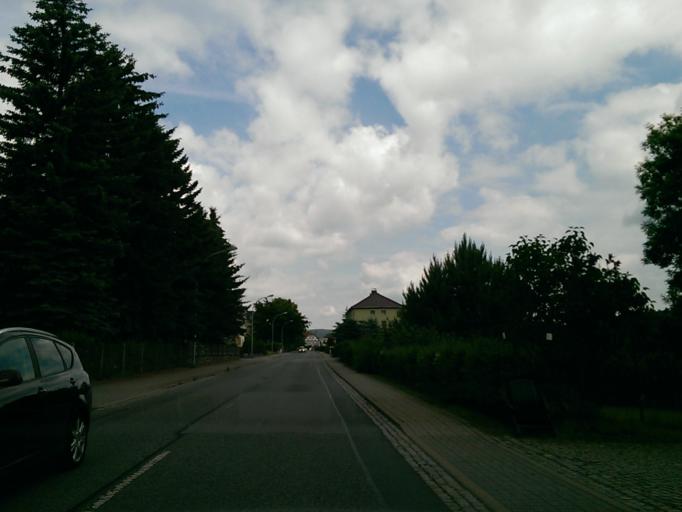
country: DE
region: Saxony
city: Hainewalde
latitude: 50.9566
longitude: 14.7224
